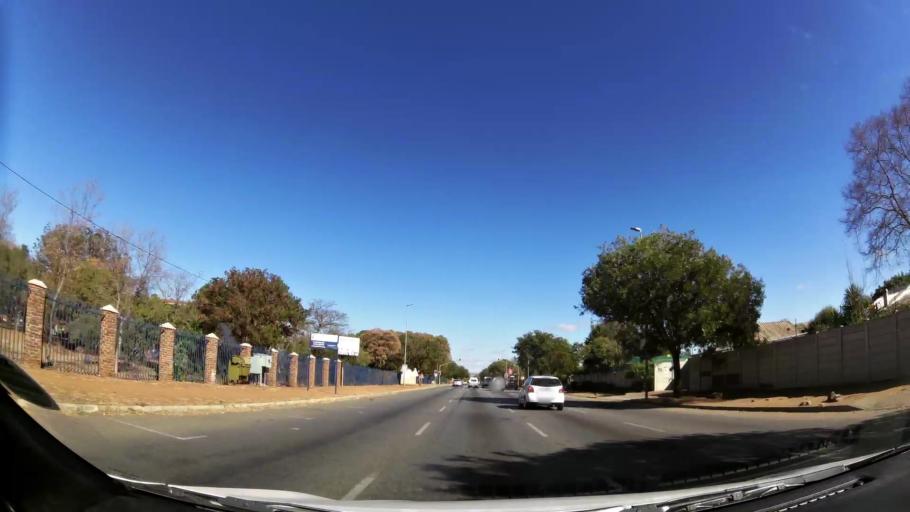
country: ZA
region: Limpopo
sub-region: Capricorn District Municipality
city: Polokwane
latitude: -23.9076
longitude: 29.4726
